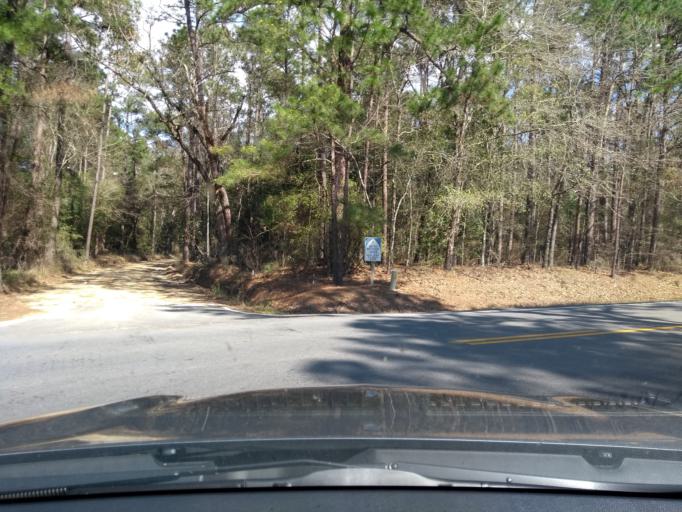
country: US
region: Georgia
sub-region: Bulloch County
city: Brooklet
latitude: 32.4868
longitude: -81.6216
